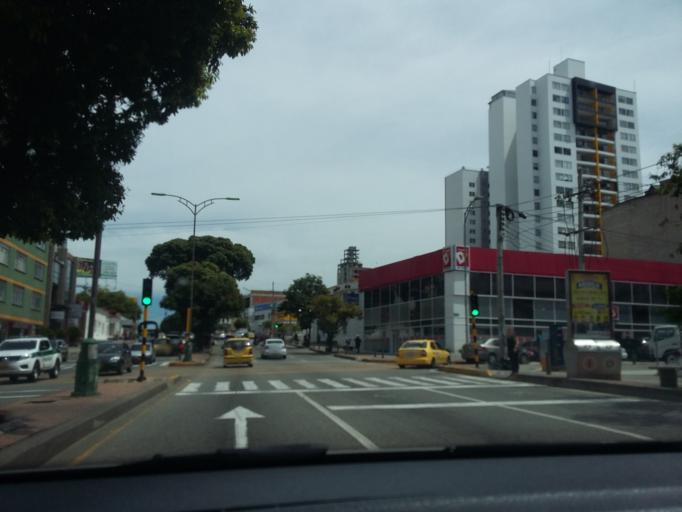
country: CO
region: Santander
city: Bucaramanga
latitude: 7.1219
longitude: -73.1166
